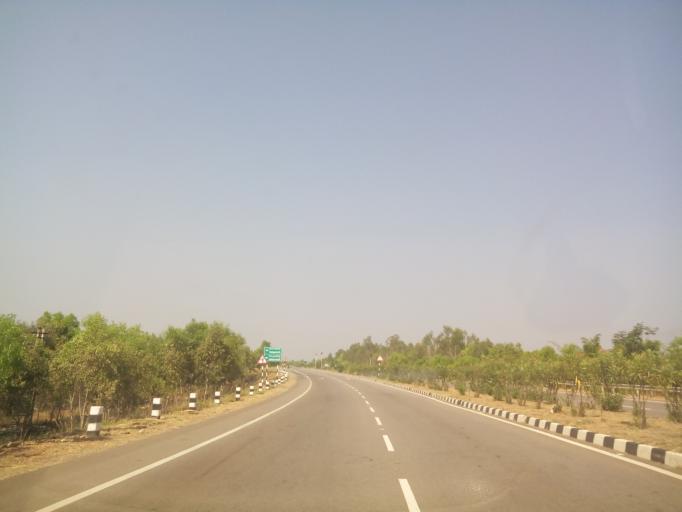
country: IN
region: Karnataka
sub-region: Mandya
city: Belluru
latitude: 12.9798
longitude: 76.8376
